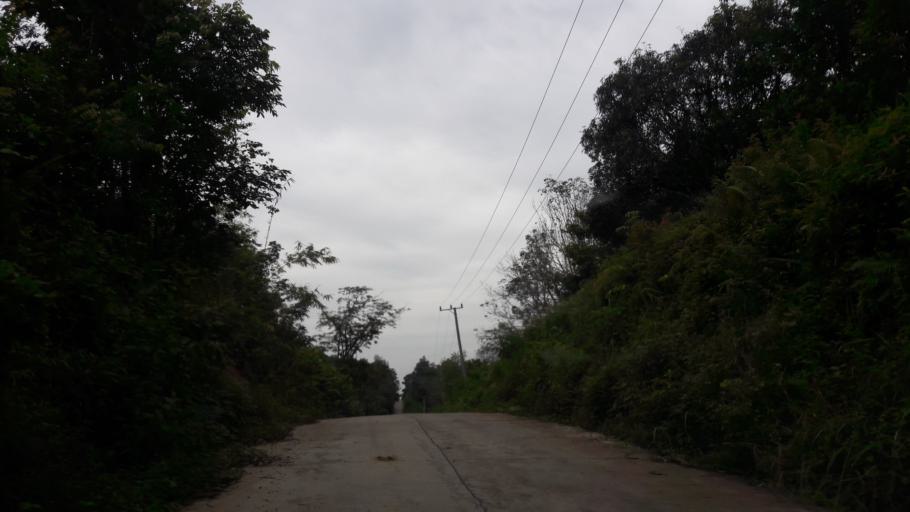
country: ID
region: South Sumatra
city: Gunungmenang
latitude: -3.1920
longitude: 103.8143
